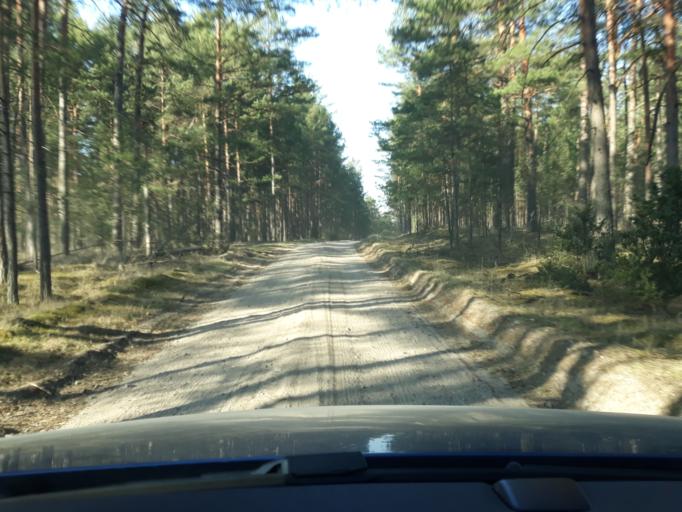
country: PL
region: Pomeranian Voivodeship
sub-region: Powiat bytowski
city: Lipnica
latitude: 53.9171
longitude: 17.4386
